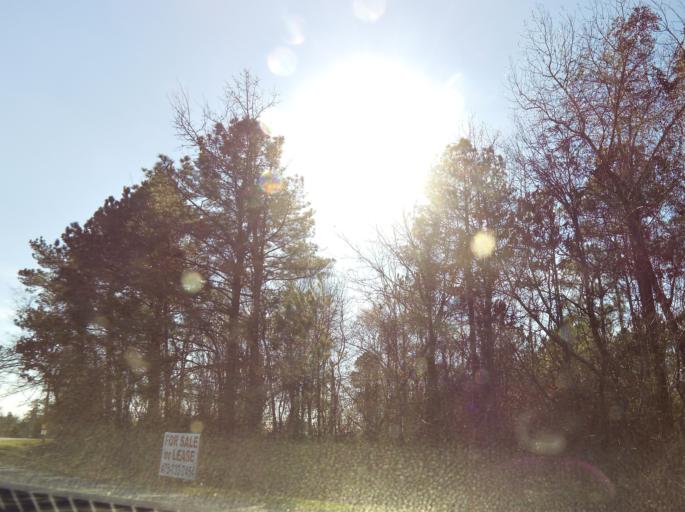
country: US
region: Georgia
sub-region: Bibb County
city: West Point
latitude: 32.8096
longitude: -83.8284
